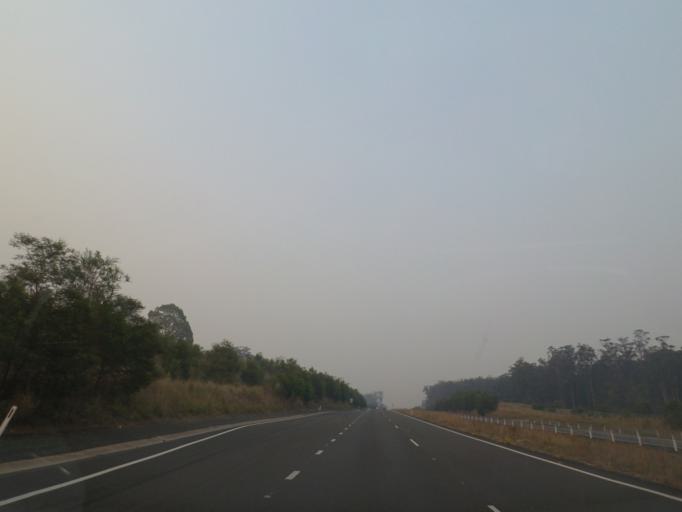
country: AU
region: New South Wales
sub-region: Nambucca Shire
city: Macksville
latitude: -30.7779
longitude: 152.8942
